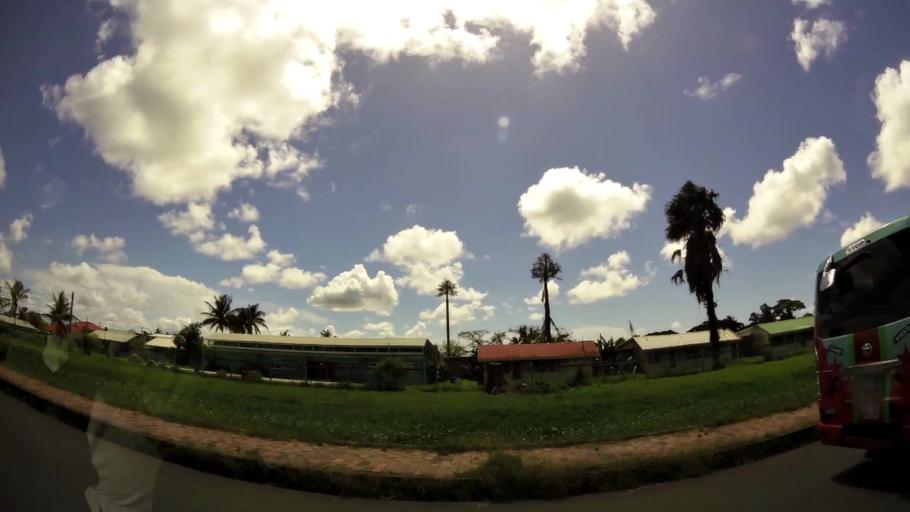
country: GY
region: Demerara-Mahaica
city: Georgetown
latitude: 6.7893
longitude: -58.1397
